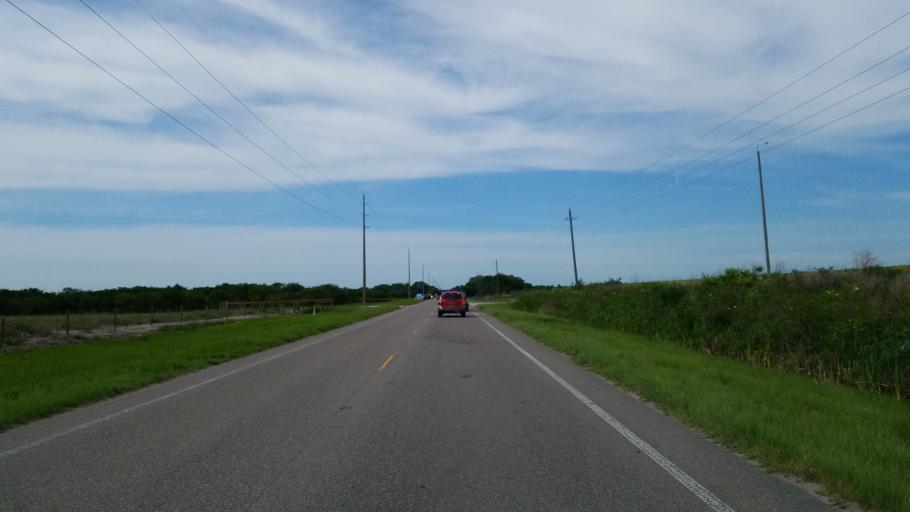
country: US
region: Florida
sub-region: Hillsborough County
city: Balm
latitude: 27.6667
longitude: -82.1462
